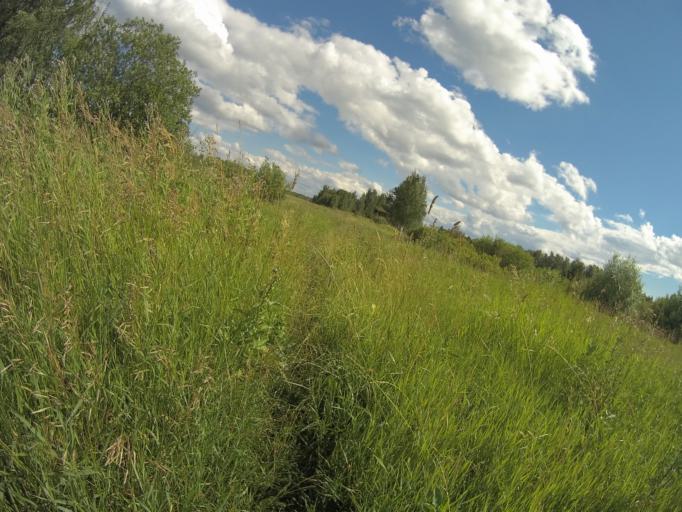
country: RU
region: Vladimir
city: Vladimir
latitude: 56.0885
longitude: 40.3783
